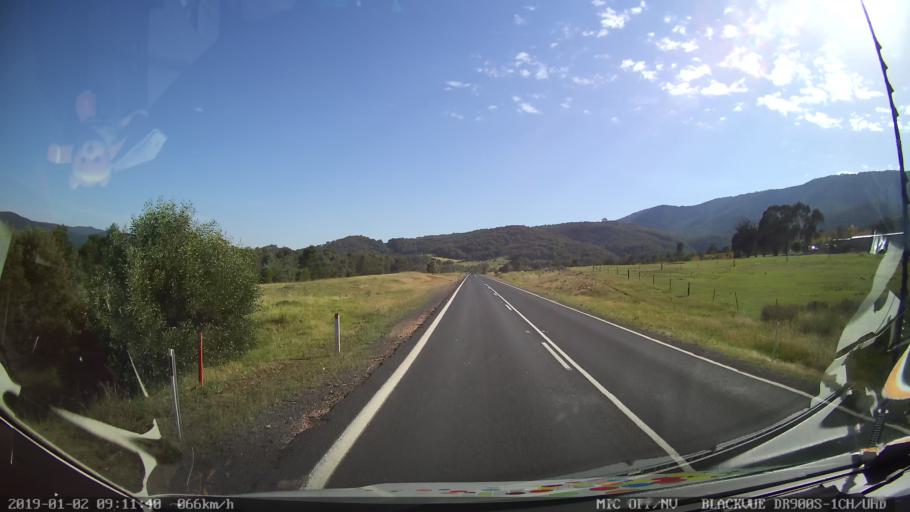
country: AU
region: New South Wales
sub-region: Tumut Shire
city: Tumut
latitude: -35.5093
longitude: 148.2699
